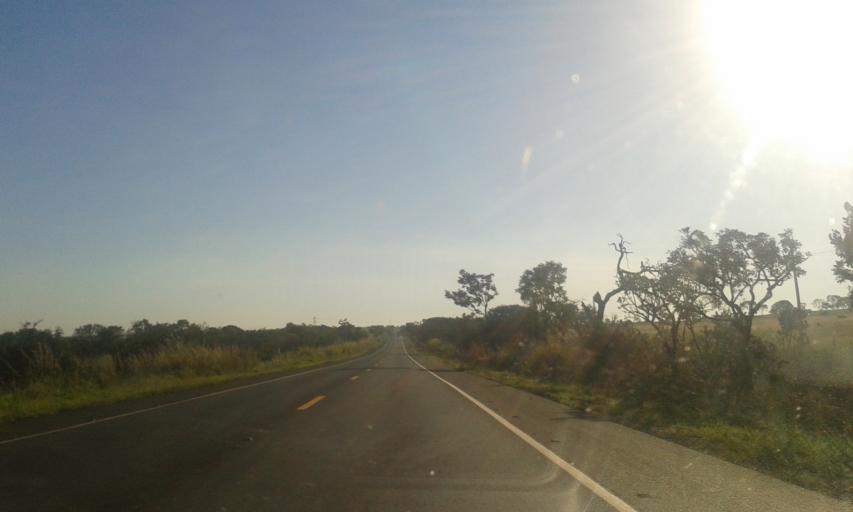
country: BR
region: Minas Gerais
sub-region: Monte Alegre De Minas
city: Monte Alegre de Minas
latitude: -18.8795
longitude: -49.1105
